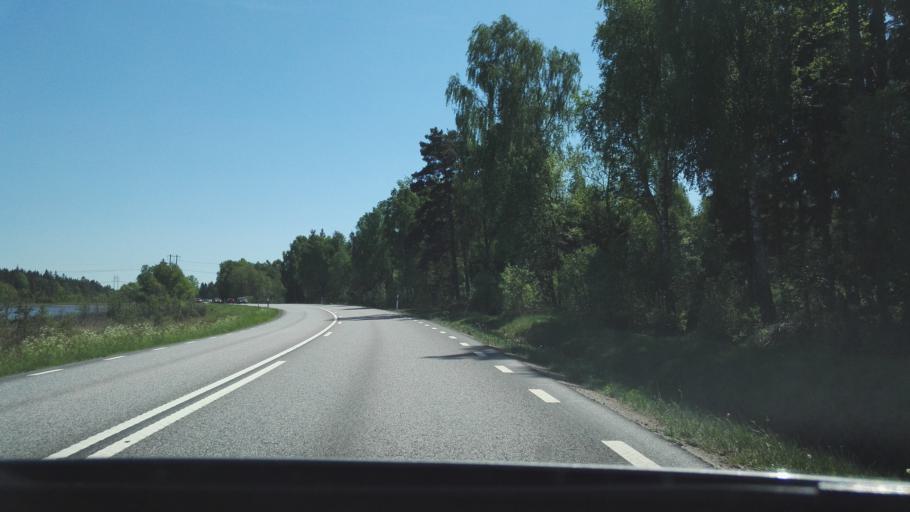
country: SE
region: Kronoberg
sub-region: Vaxjo Kommun
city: Vaexjoe
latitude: 56.8316
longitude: 14.8668
